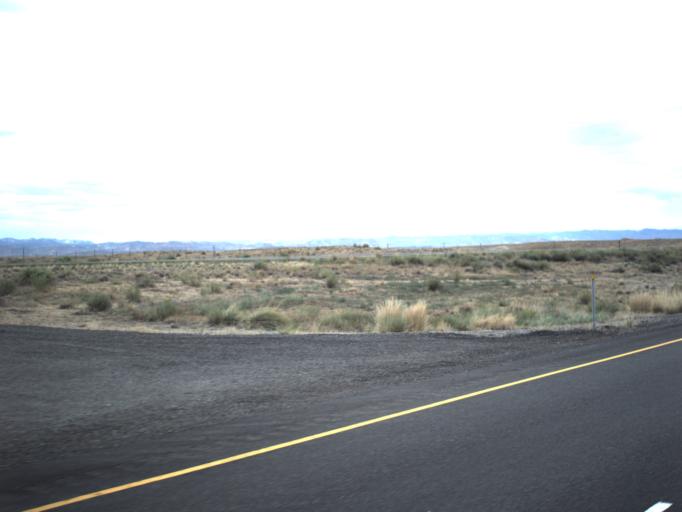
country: US
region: Colorado
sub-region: Mesa County
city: Loma
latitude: 39.0309
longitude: -109.2893
